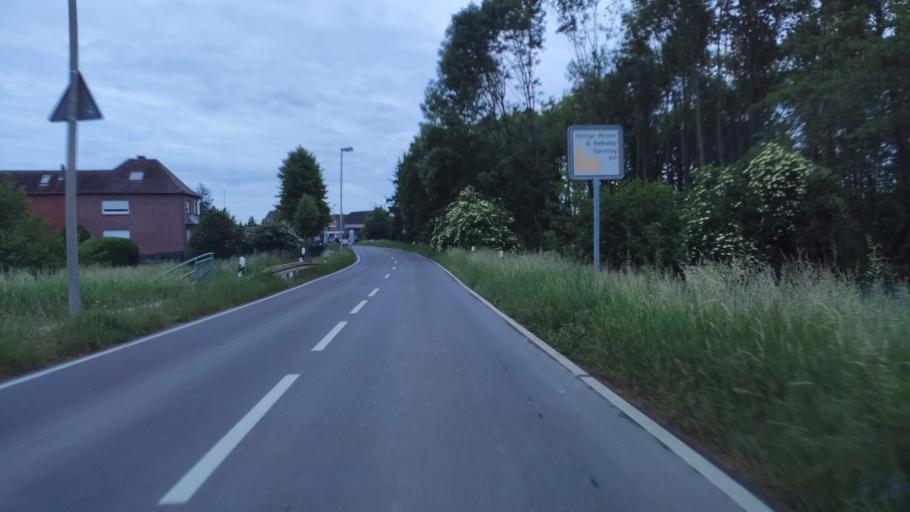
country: DE
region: North Rhine-Westphalia
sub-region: Regierungsbezirk Dusseldorf
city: Dormagen
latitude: 51.1109
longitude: 6.7461
